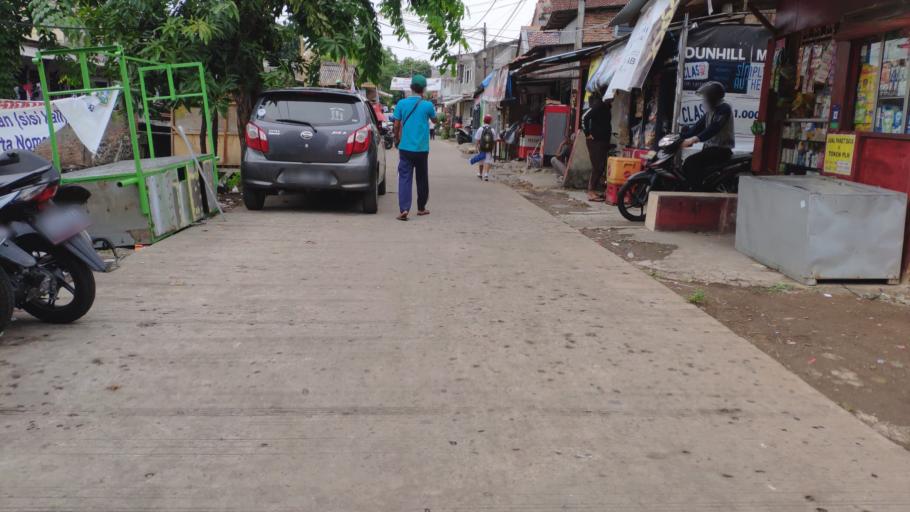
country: ID
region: Jakarta Raya
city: Jakarta
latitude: -6.2045
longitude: 106.8601
